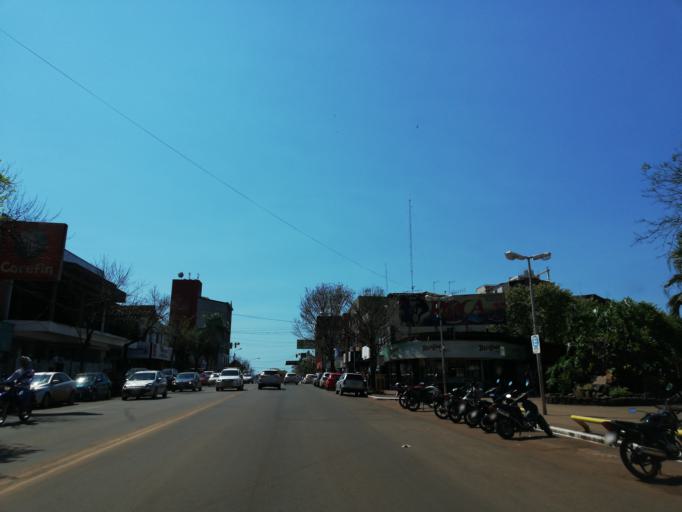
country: AR
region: Misiones
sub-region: Departamento de Eldorado
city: Eldorado
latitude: -26.4084
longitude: -54.6073
